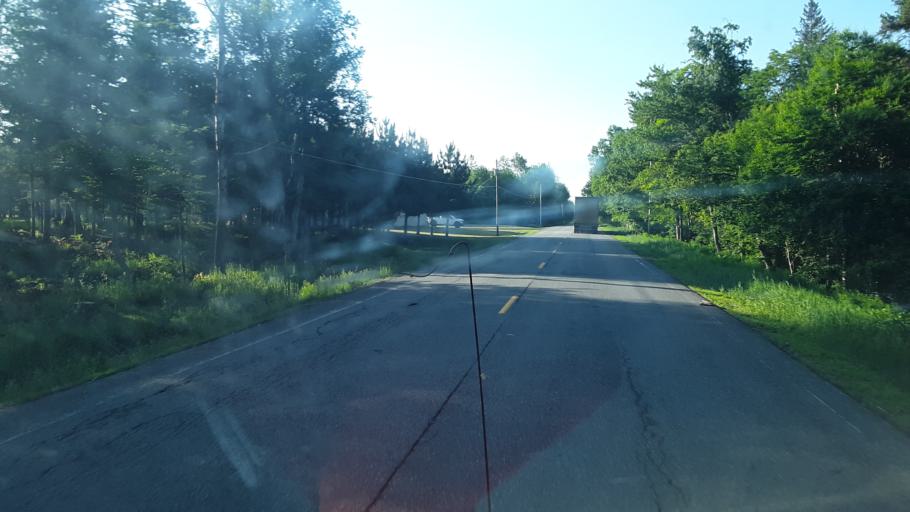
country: US
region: Maine
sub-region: Penobscot County
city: Patten
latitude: 46.1839
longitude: -68.2510
